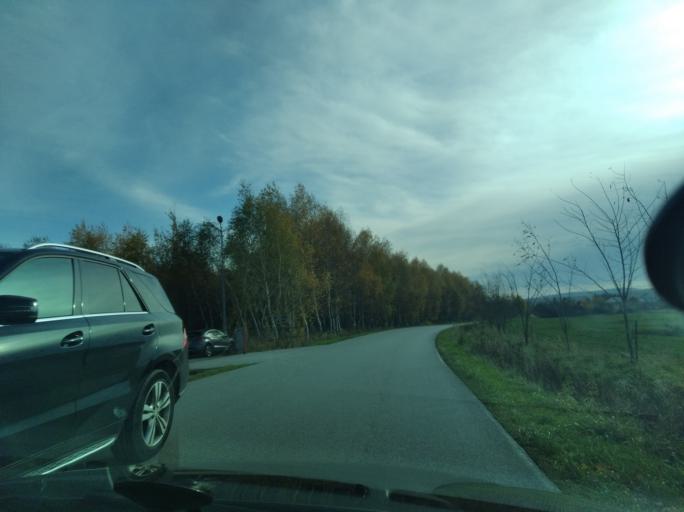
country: PL
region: Subcarpathian Voivodeship
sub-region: Powiat lancucki
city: Kraczkowa
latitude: 50.0429
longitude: 22.1322
